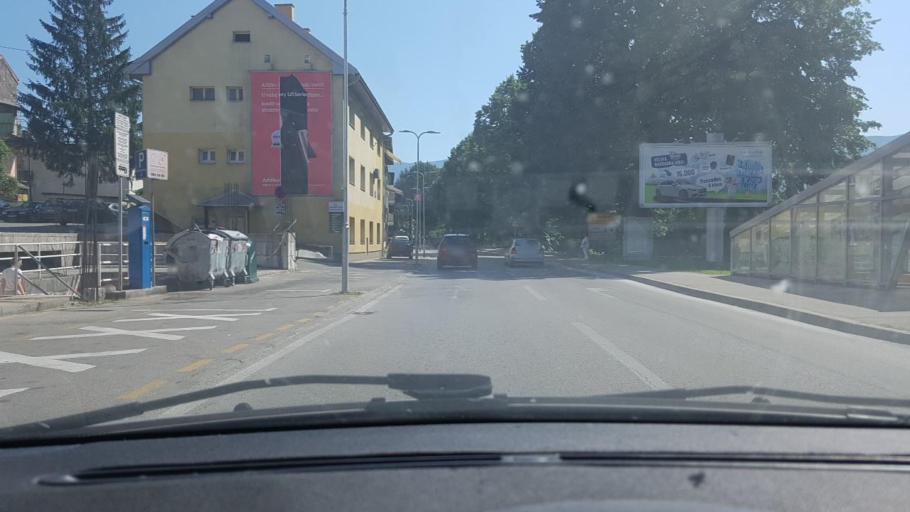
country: BA
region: Federation of Bosnia and Herzegovina
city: Bihac
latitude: 44.8149
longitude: 15.8680
